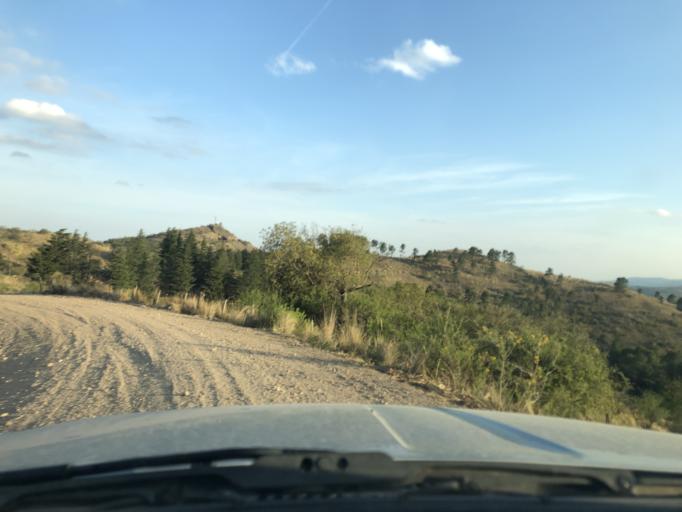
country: AR
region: Cordoba
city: Agua de Oro
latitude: -31.0593
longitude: -64.3498
